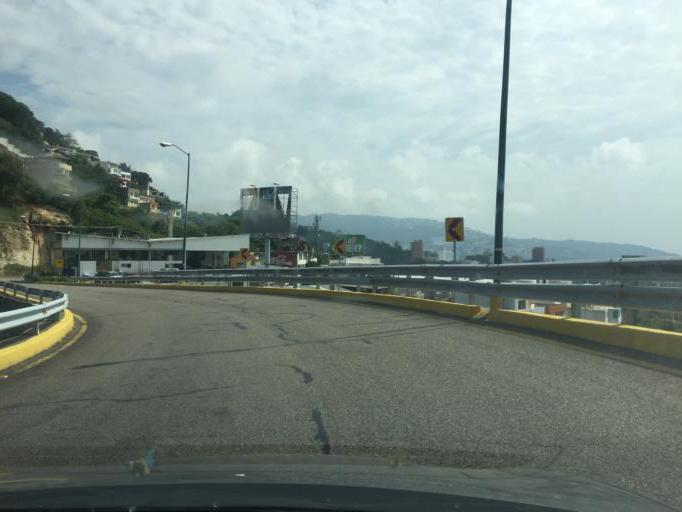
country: MX
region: Guerrero
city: Acapulco de Juarez
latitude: 16.8712
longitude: -99.8701
